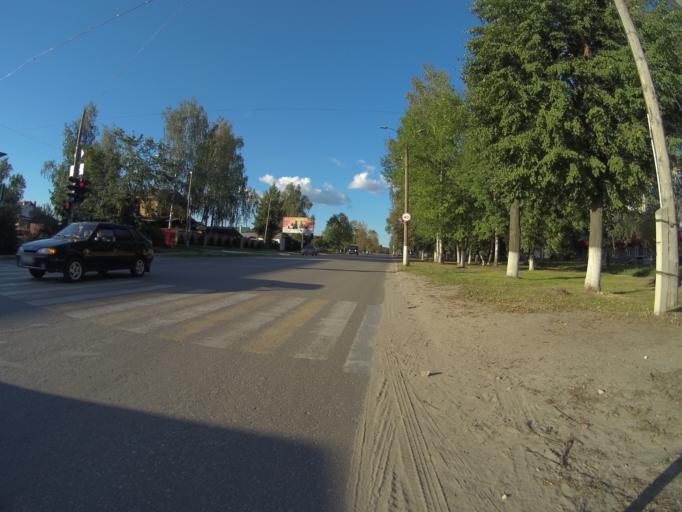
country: RU
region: Vladimir
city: Gus'-Khrustal'nyy
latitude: 55.6209
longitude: 40.6787
